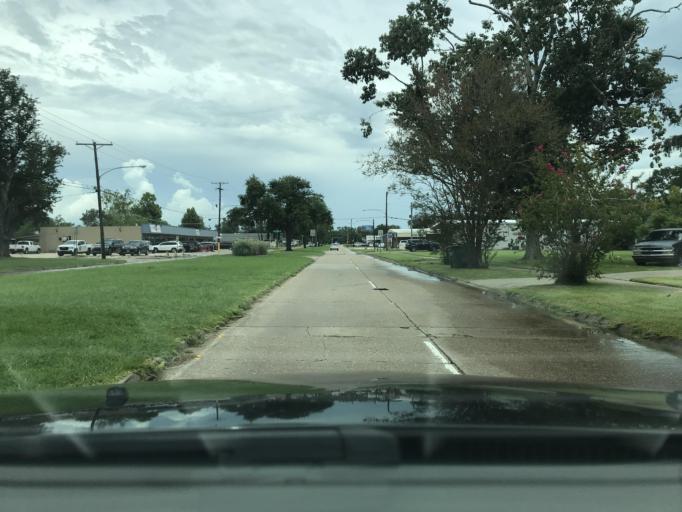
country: US
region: Louisiana
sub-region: Calcasieu Parish
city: Lake Charles
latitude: 30.2096
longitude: -93.2042
